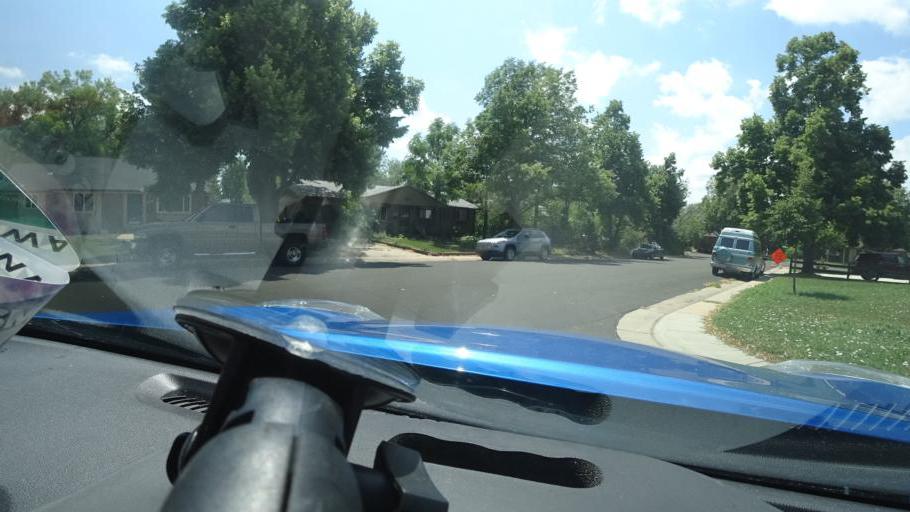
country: US
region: Colorado
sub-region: Adams County
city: Aurora
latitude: 39.7105
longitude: -104.8520
